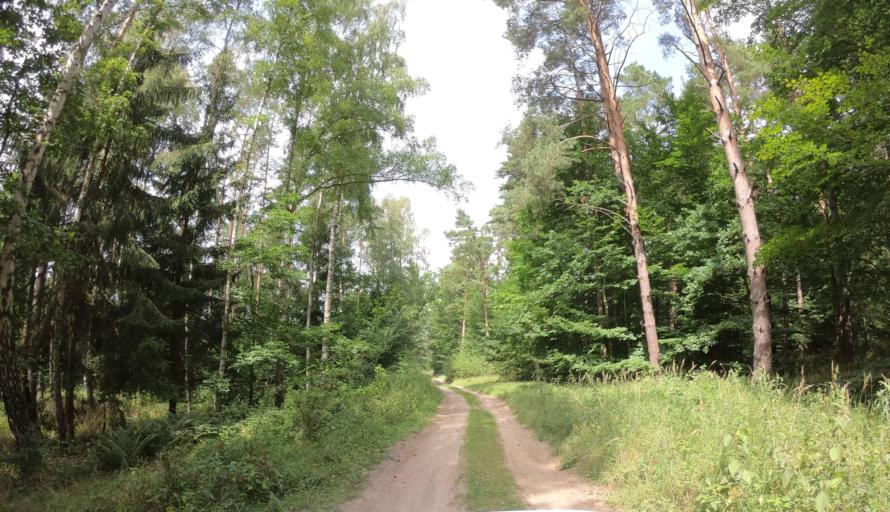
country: PL
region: West Pomeranian Voivodeship
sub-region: Powiat gryfinski
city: Stare Czarnowo
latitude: 53.3313
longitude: 14.8086
